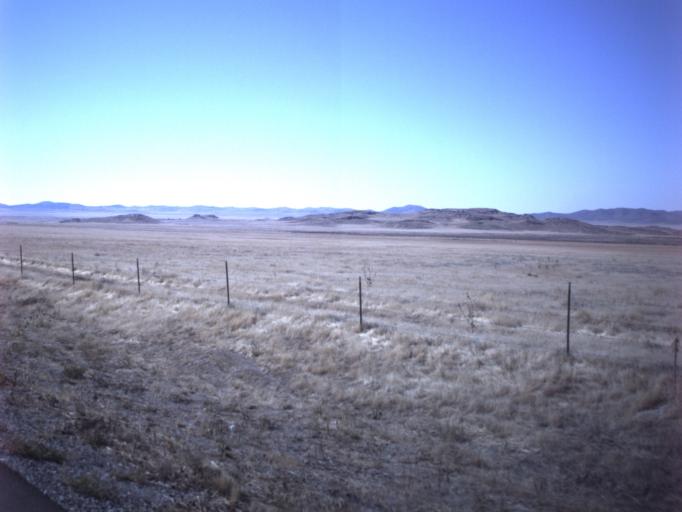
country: US
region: Utah
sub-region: Tooele County
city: Grantsville
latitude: 40.4136
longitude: -112.7486
